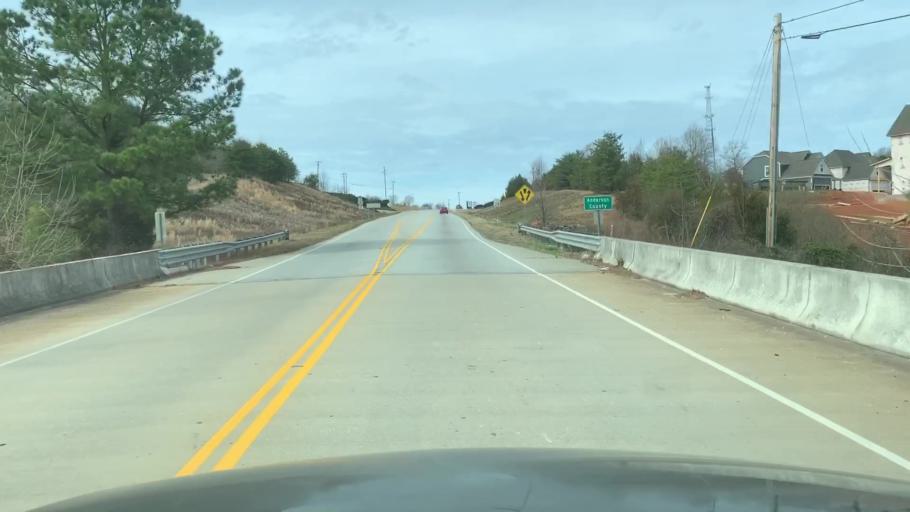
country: US
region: South Carolina
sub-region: Greenville County
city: Golden Grove
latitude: 34.7651
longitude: -82.4552
